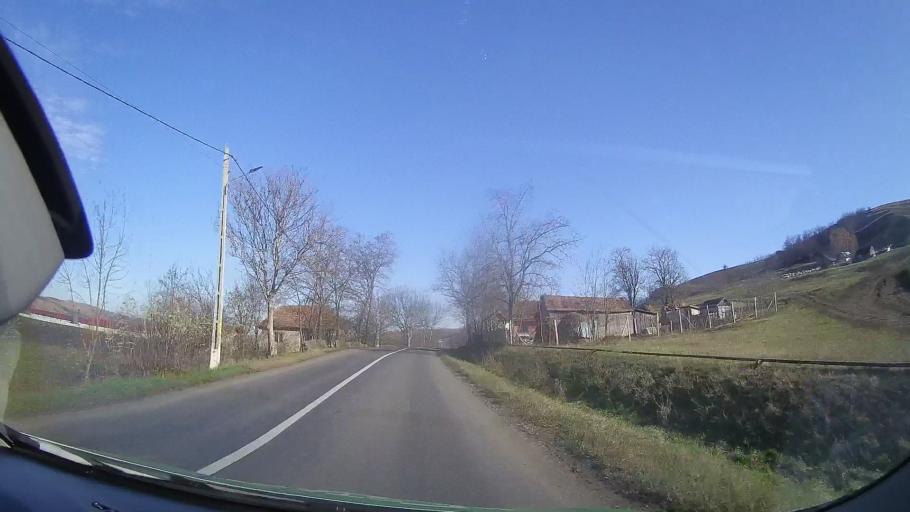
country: RO
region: Mures
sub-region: Comuna Iclanzel
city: Iclanzel
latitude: 46.5486
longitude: 24.3266
